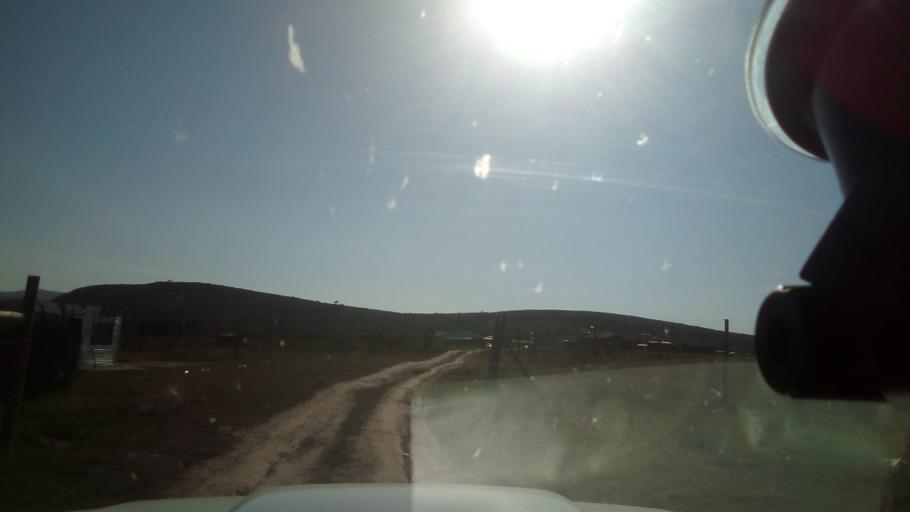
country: ZA
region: Eastern Cape
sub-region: Buffalo City Metropolitan Municipality
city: Bhisho
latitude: -32.8219
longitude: 27.3540
